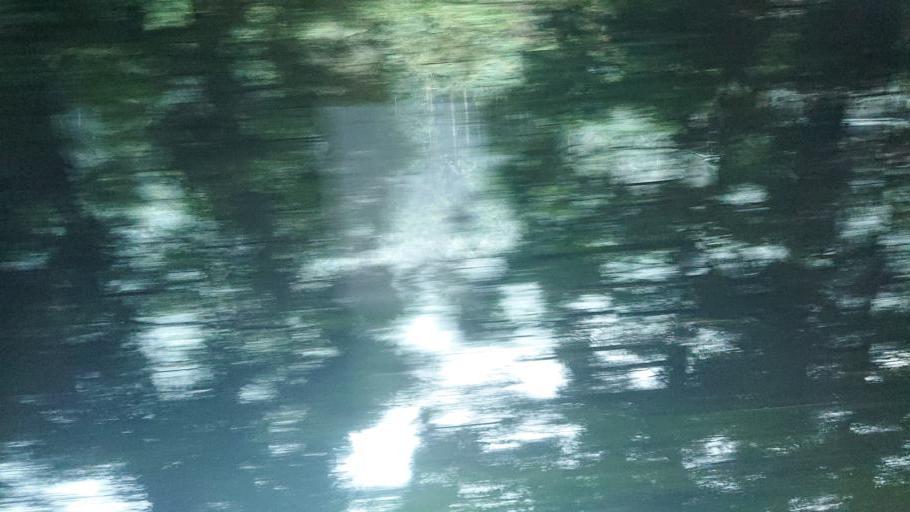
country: TW
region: Taiwan
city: Lugu
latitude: 23.5172
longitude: 120.7009
